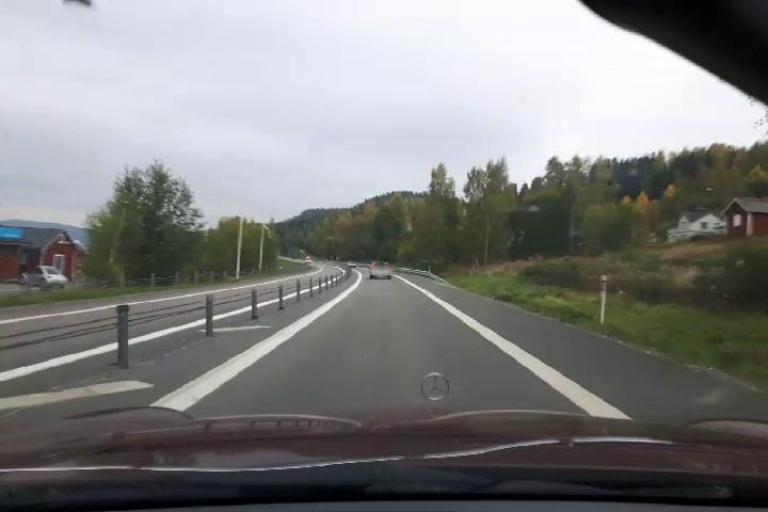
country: SE
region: Vaesternorrland
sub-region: Kramfors Kommun
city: Nordingra
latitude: 63.0472
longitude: 18.3258
